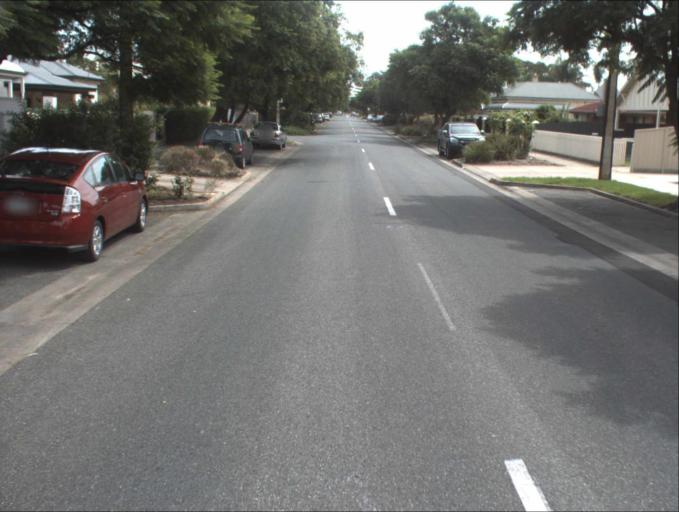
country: AU
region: South Australia
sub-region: Port Adelaide Enfield
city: Alberton
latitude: -34.8583
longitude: 138.5206
